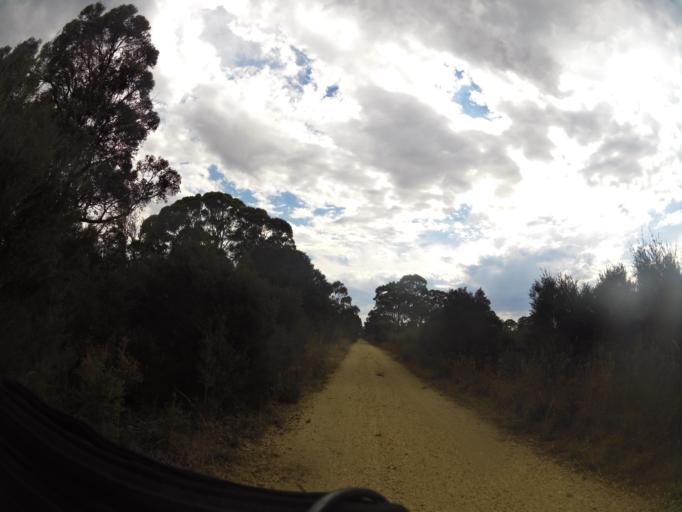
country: AU
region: Victoria
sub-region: Wellington
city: Heyfield
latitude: -38.0433
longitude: 146.6422
